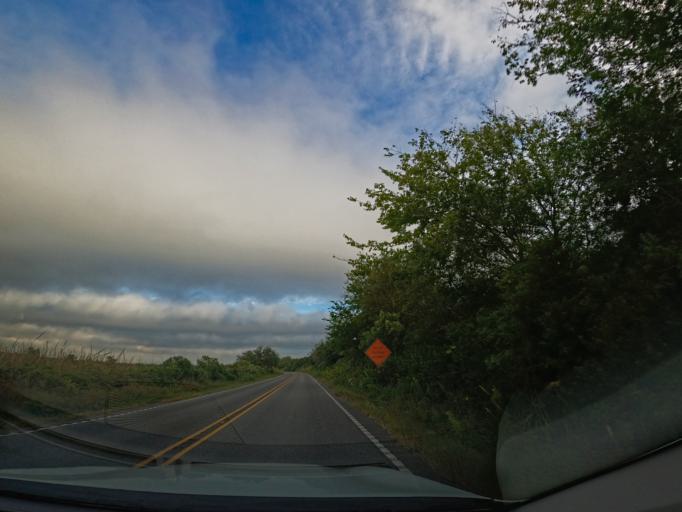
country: US
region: Louisiana
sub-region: Terrebonne Parish
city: Dulac
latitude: 29.3555
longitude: -90.7013
